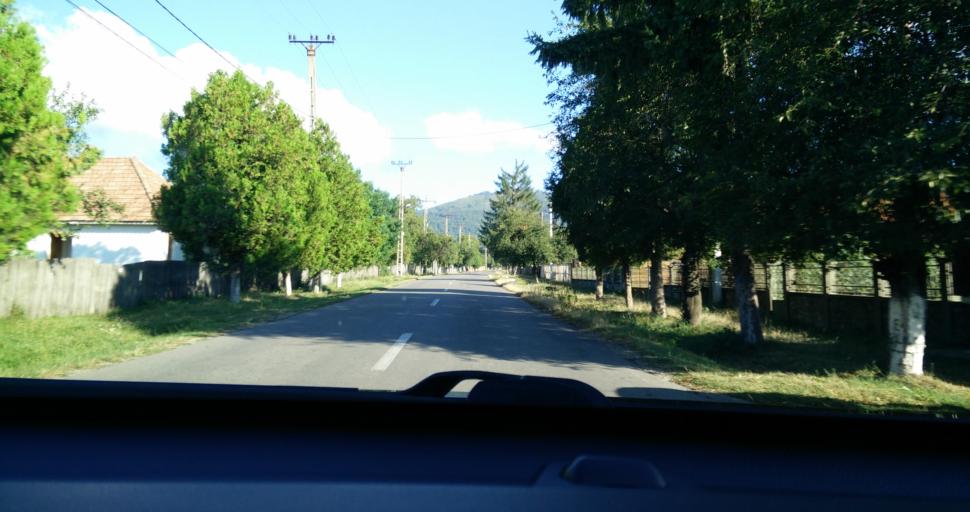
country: RO
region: Gorj
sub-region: Comuna Polovragi
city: Polovragi
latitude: 45.1737
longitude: 23.8015
